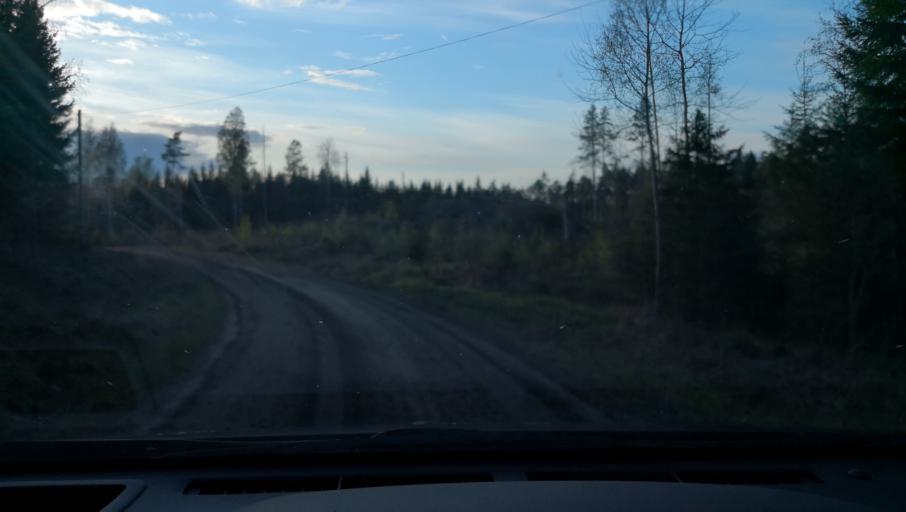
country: SE
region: OErebro
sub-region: Askersunds Kommun
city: Asbro
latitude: 58.8876
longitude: 15.1211
